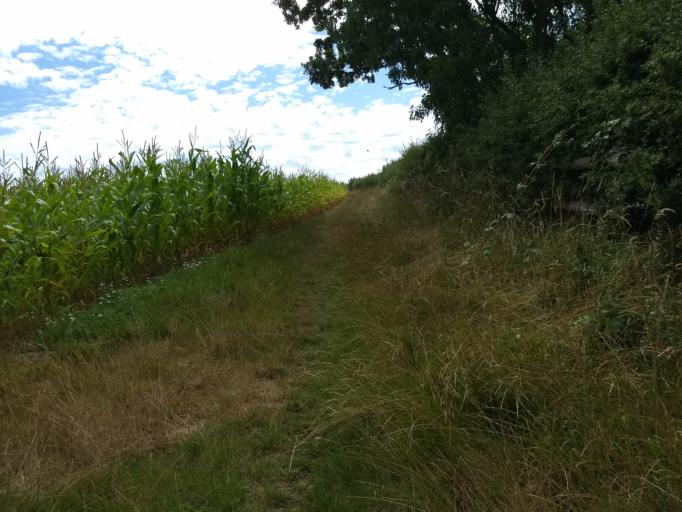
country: GB
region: England
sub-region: Isle of Wight
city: Newport
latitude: 50.7086
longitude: -1.2695
